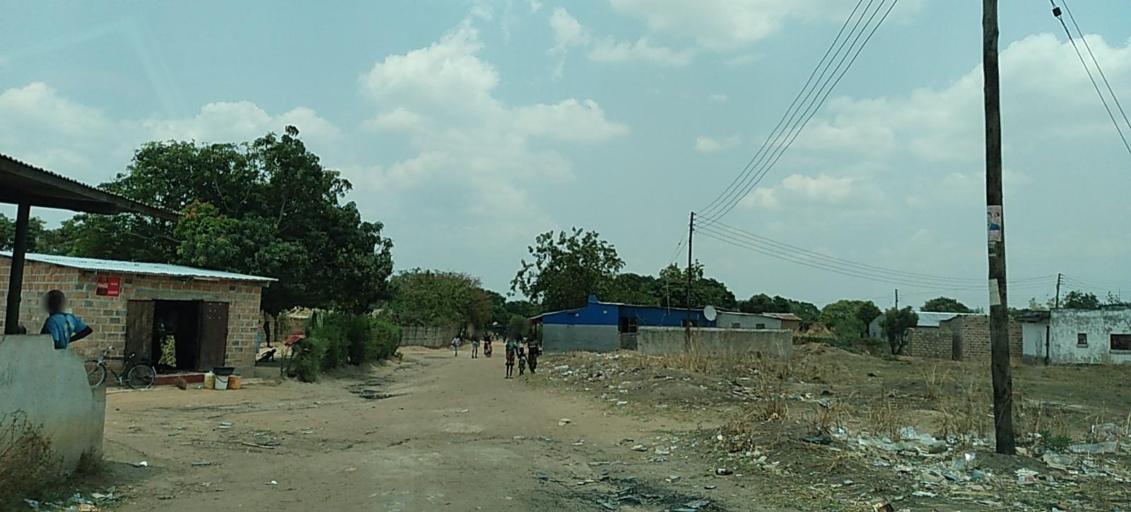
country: ZM
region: Copperbelt
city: Luanshya
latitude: -13.1204
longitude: 28.3095
